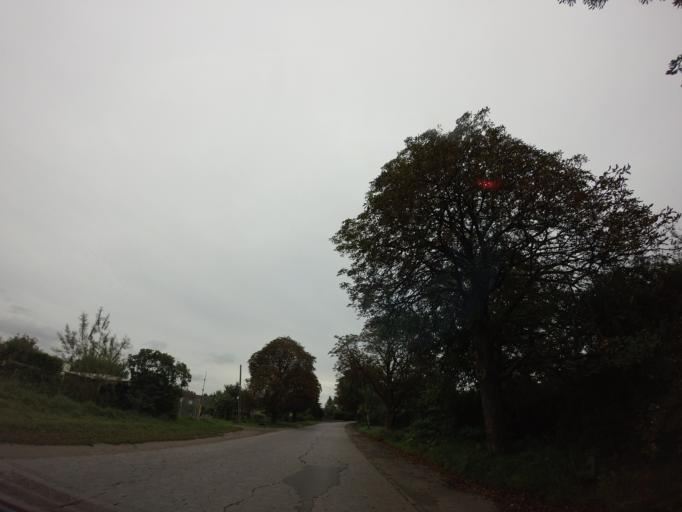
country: PL
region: West Pomeranian Voivodeship
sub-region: Powiat policki
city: Przeclaw
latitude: 53.4413
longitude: 14.4704
